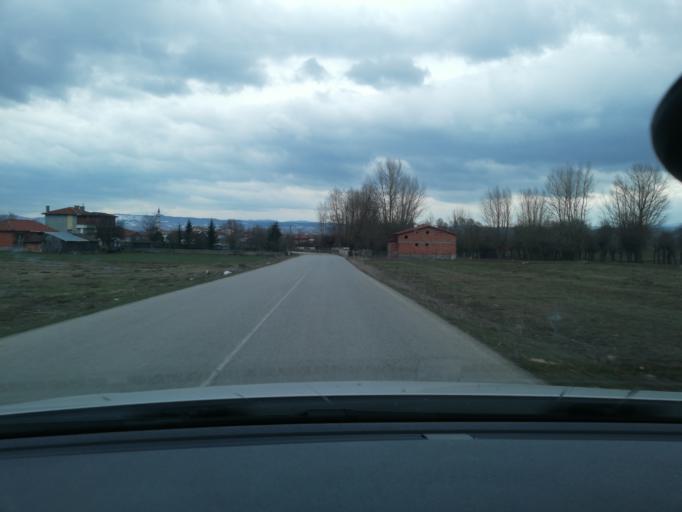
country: TR
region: Bolu
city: Gerede
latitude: 40.7368
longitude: 32.2112
